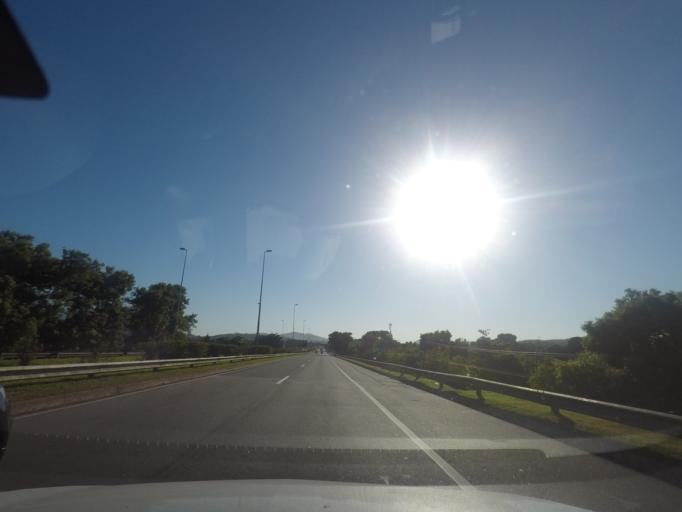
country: BR
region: Rio de Janeiro
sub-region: Petropolis
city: Petropolis
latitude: -22.6474
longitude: -43.2229
